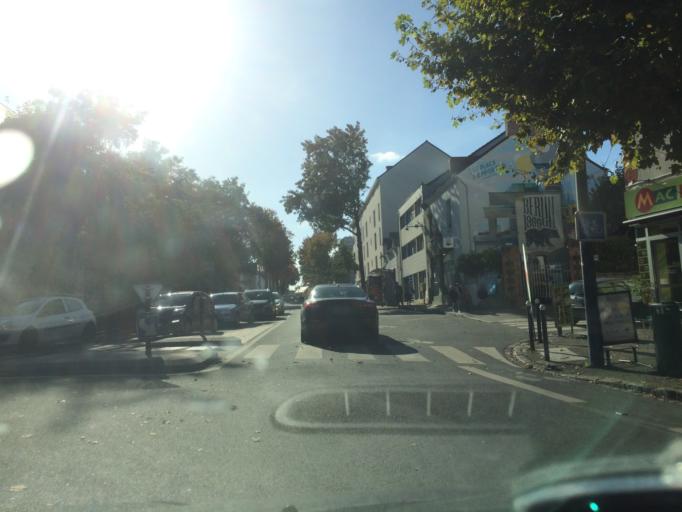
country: FR
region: Pays de la Loire
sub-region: Departement de la Loire-Atlantique
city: Nantes
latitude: 47.2411
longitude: -1.5568
